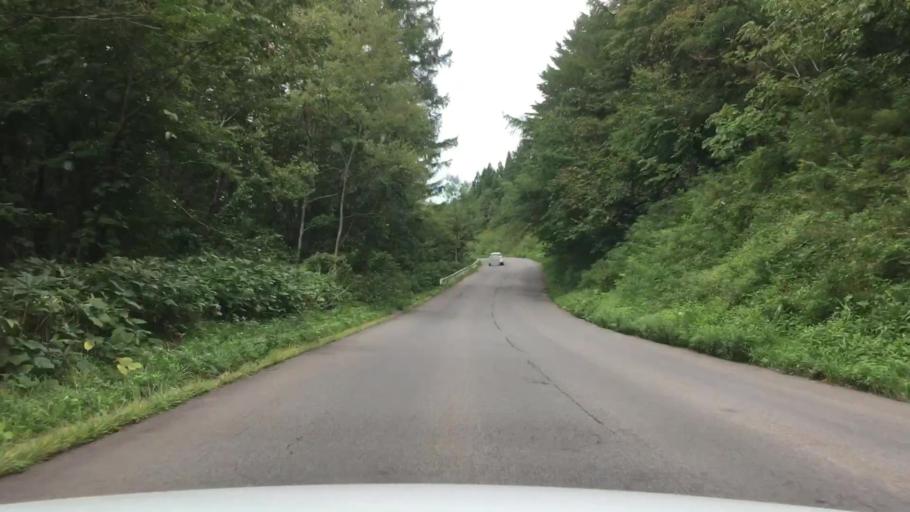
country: JP
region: Aomori
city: Shimokizukuri
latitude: 40.7183
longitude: 140.2592
